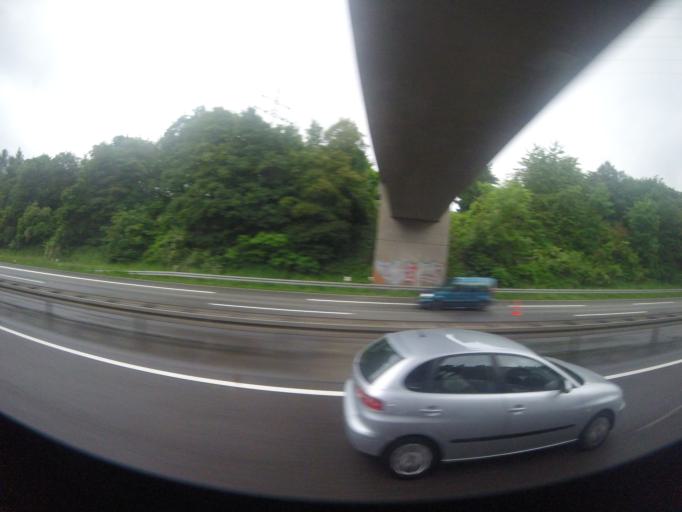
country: DE
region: Saarland
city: Merchweiler
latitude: 49.3425
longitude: 7.0497
